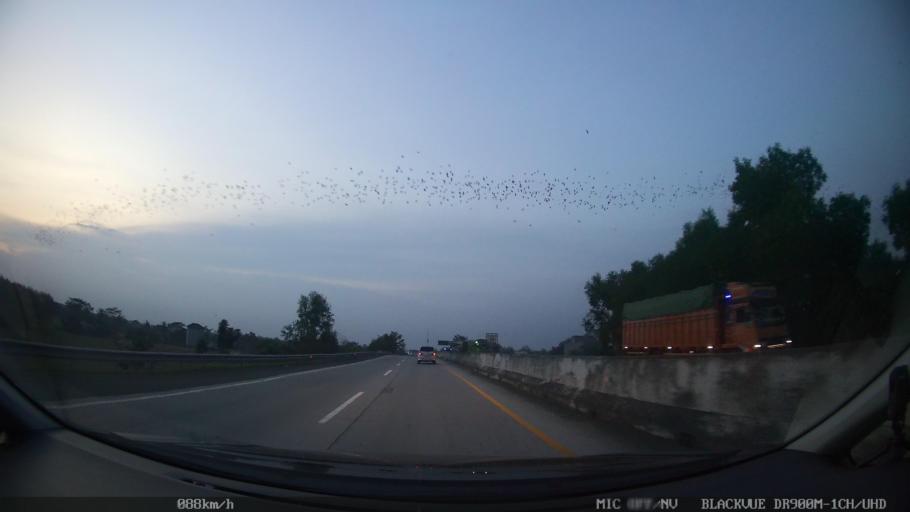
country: ID
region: Lampung
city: Sidorejo
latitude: -5.6022
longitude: 105.5544
